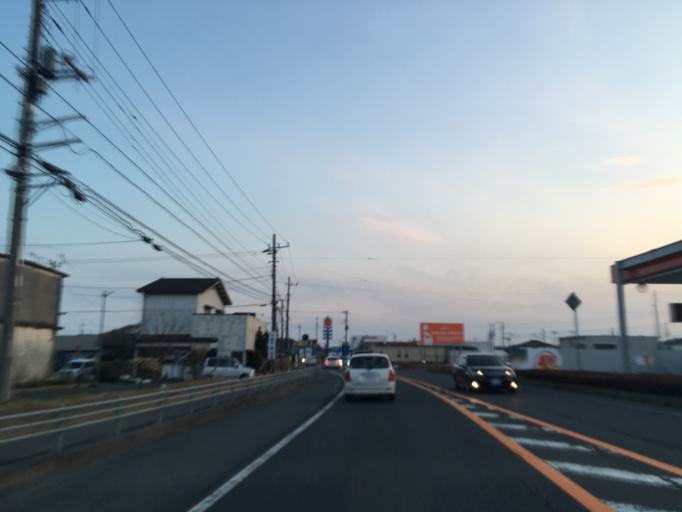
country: JP
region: Ibaraki
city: Kitaibaraki
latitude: 36.7765
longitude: 140.7405
